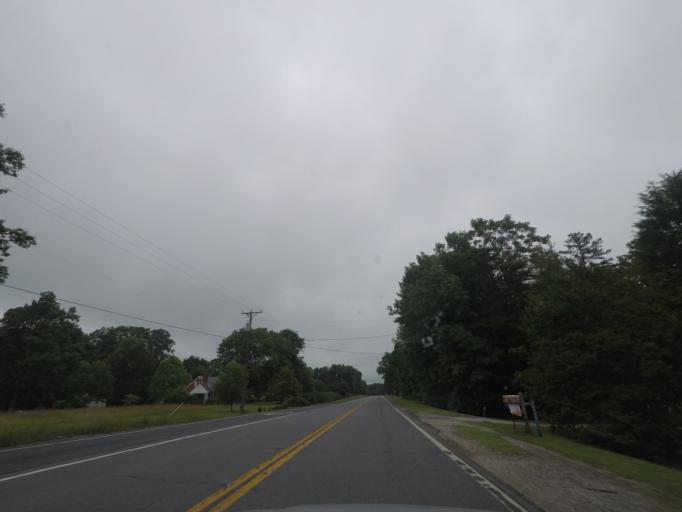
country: US
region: Virginia
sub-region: Fluvanna County
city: Weber City
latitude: 37.6517
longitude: -78.3547
